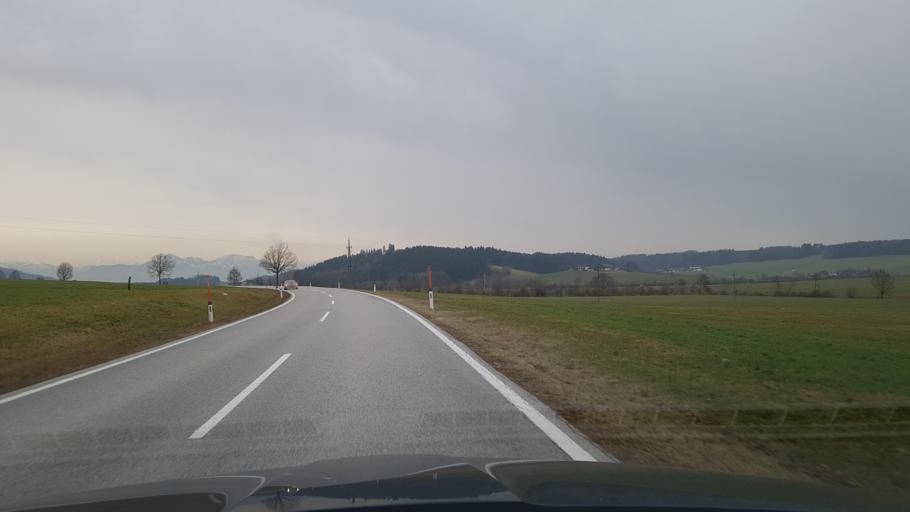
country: AT
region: Salzburg
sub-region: Politischer Bezirk Salzburg-Umgebung
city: Nussdorf am Haunsberg
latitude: 47.9857
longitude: 13.0139
